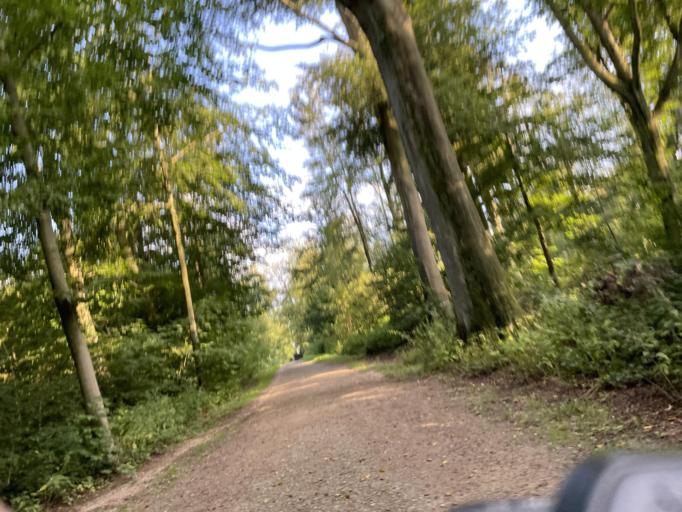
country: DE
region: North Rhine-Westphalia
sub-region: Regierungsbezirk Dusseldorf
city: Essen
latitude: 51.4138
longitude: 7.0503
